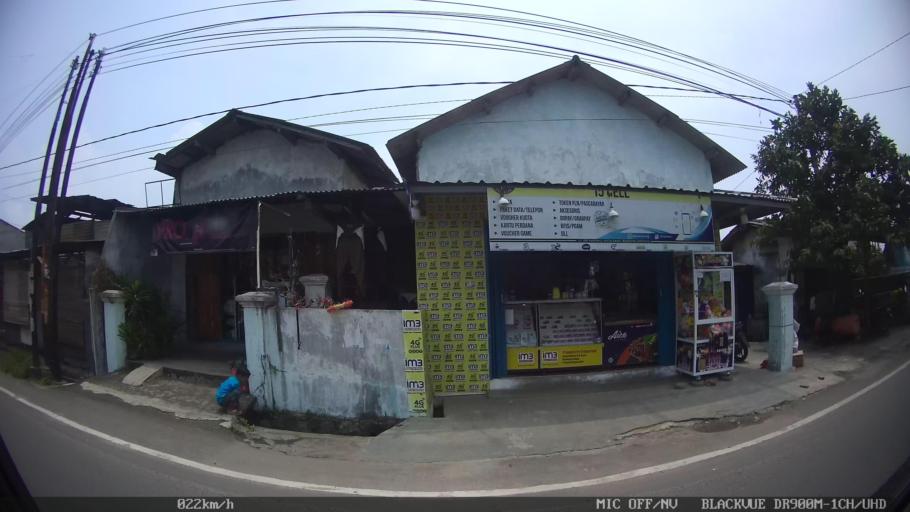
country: ID
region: Lampung
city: Bandarlampung
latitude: -5.4183
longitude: 105.2737
